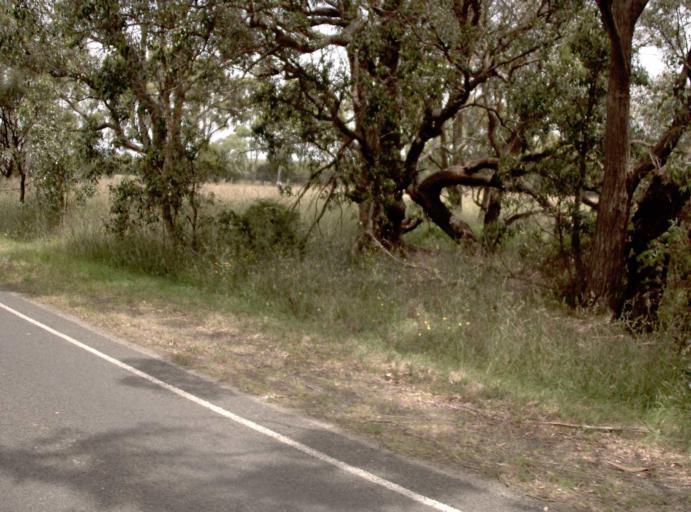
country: AU
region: Victoria
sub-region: Latrobe
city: Traralgon
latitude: -38.4907
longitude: 146.7133
